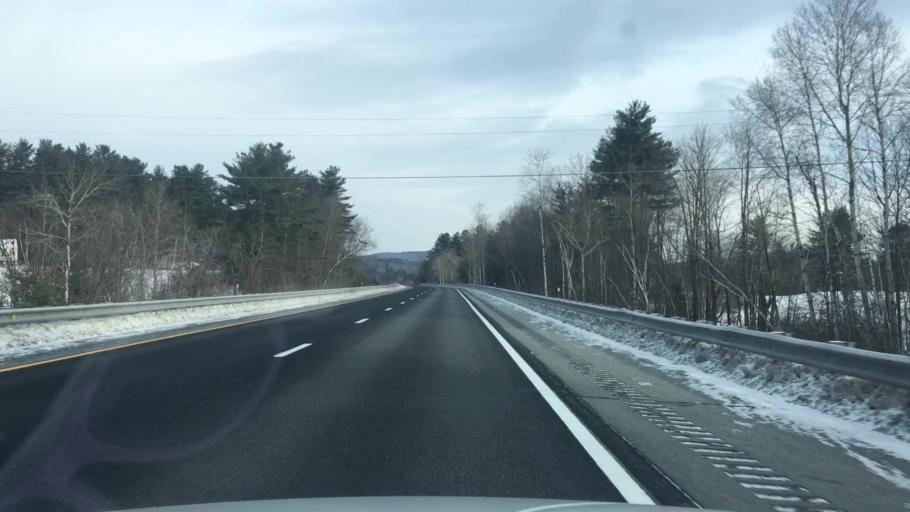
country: US
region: New Hampshire
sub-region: Sullivan County
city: Grantham
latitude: 43.5297
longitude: -72.1400
